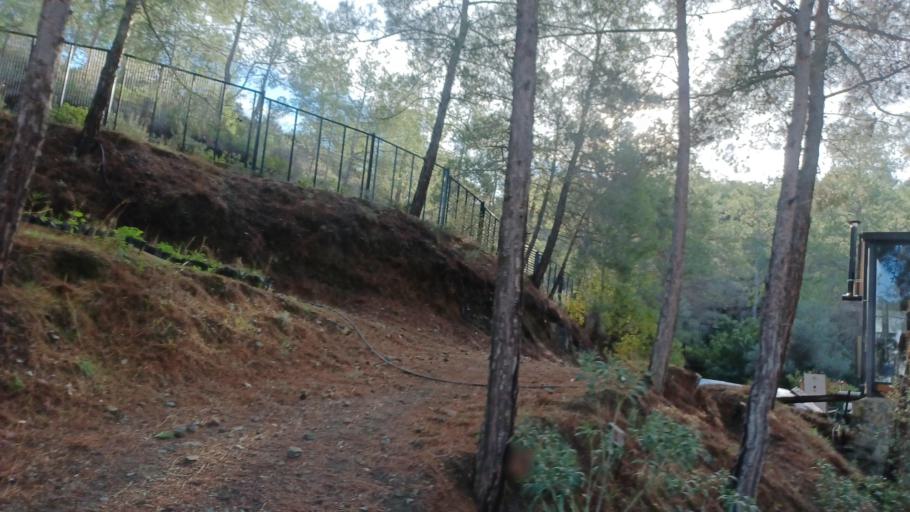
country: CY
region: Lefkosia
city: Lythrodontas
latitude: 34.9210
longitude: 33.2963
